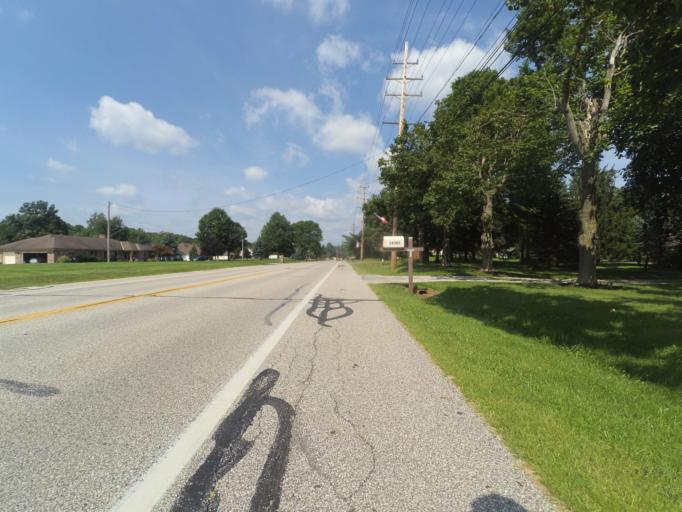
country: US
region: Ohio
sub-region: Cuyahoga County
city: Walton Hills
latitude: 41.3582
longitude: -81.5821
